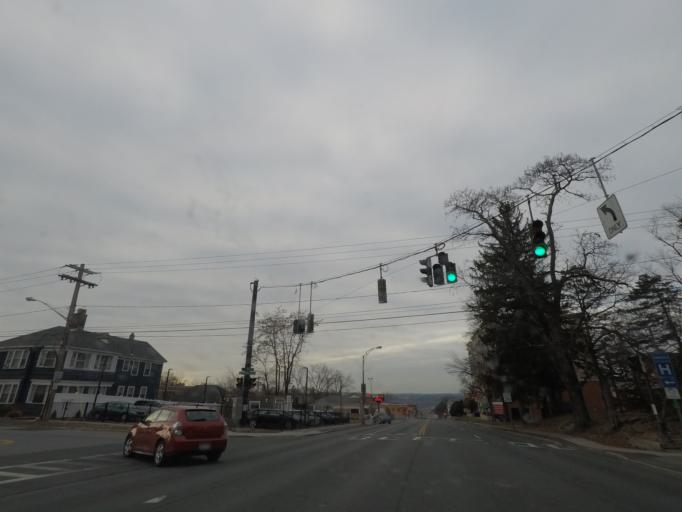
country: US
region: New York
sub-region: Albany County
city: Green Island
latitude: 42.7383
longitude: -73.6699
